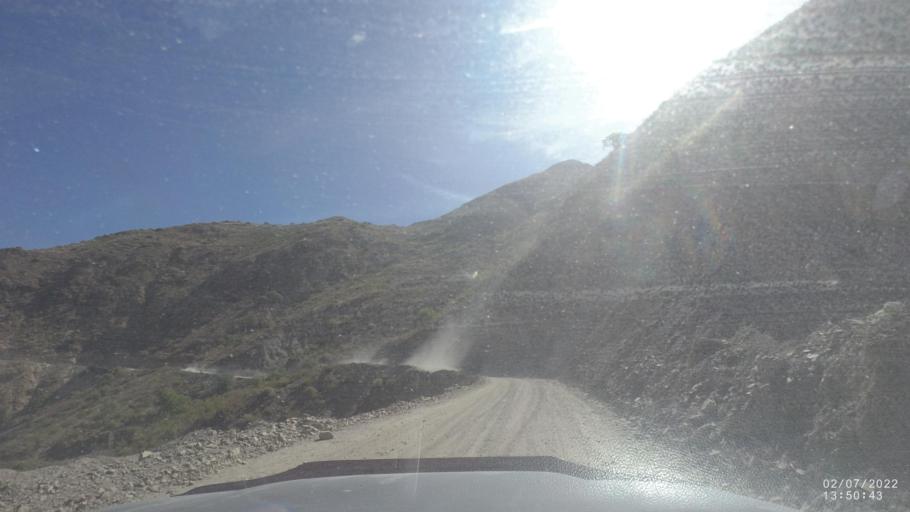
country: BO
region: Cochabamba
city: Irpa Irpa
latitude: -17.8221
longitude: -66.3789
